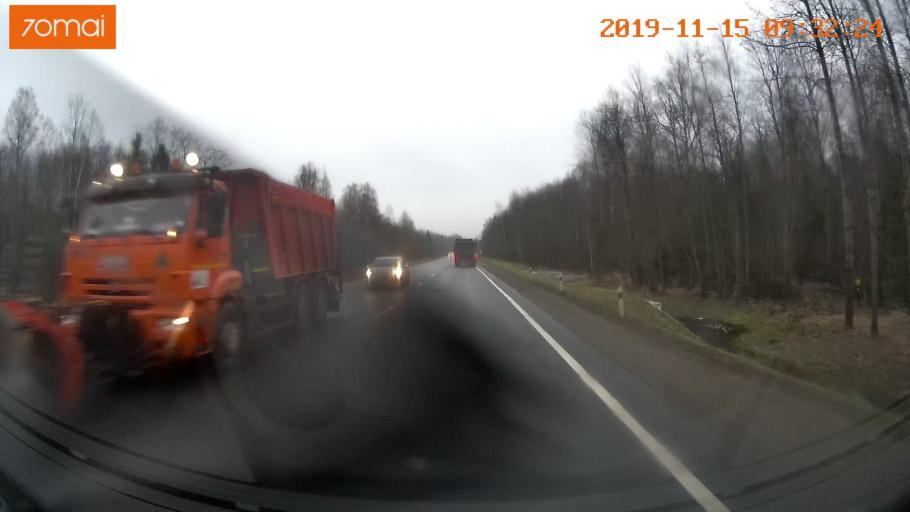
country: RU
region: Vologda
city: Sheksna
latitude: 59.2717
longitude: 38.3341
